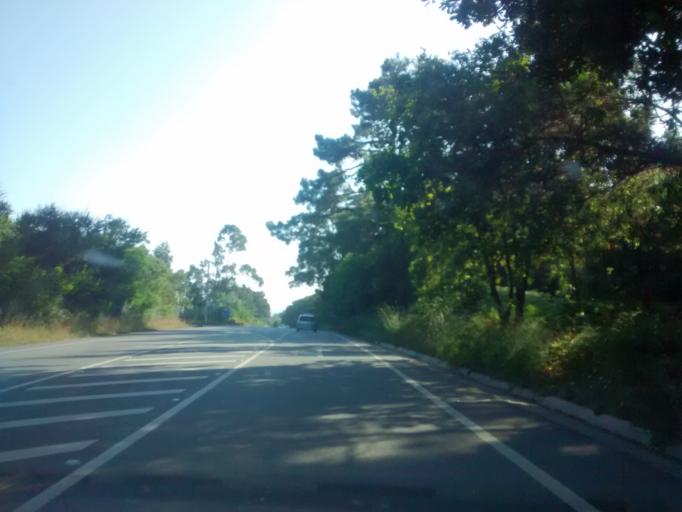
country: PT
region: Viana do Castelo
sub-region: Caminha
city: Vila Praia de Ancora
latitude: 41.7935
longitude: -8.8649
